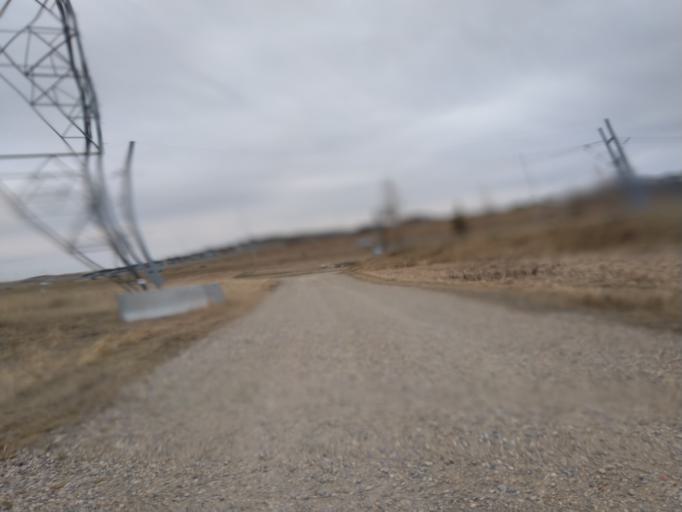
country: CA
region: Alberta
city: Calgary
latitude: 51.1685
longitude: -114.1070
